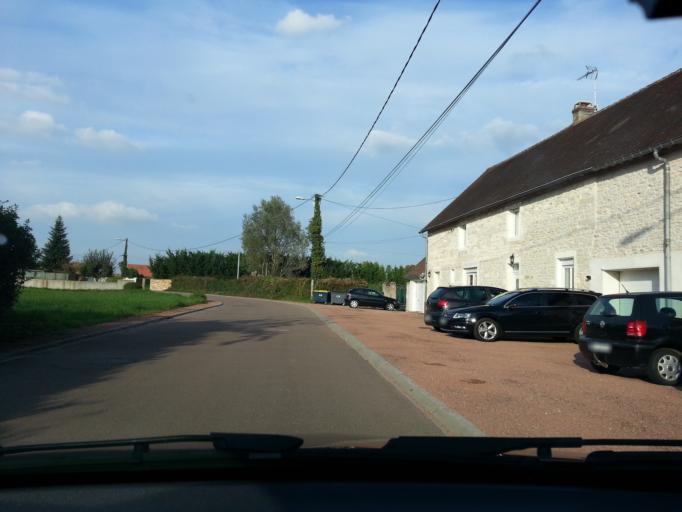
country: FR
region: Bourgogne
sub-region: Departement de Saone-et-Loire
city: Chatenoy-le-Royal
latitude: 46.7769
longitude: 4.8047
